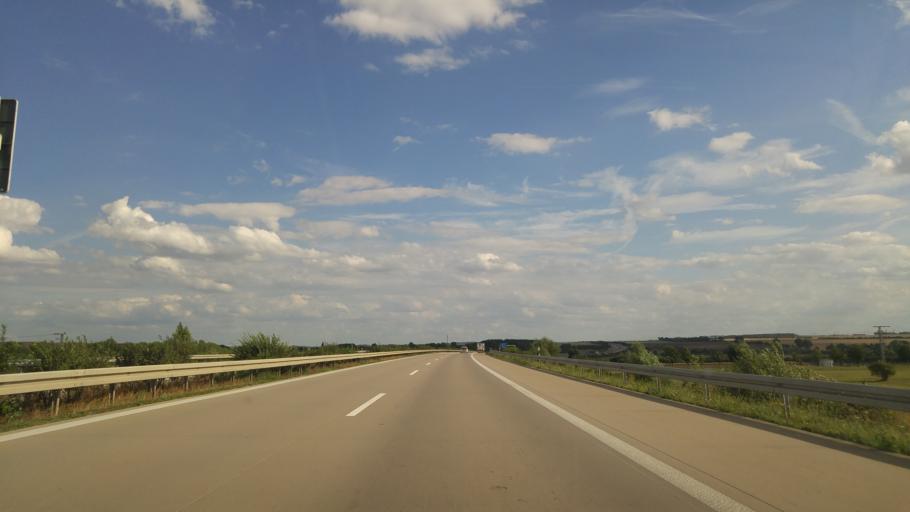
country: DE
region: Saxony-Anhalt
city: Bad Lauchstadt
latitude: 51.3862
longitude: 11.9092
